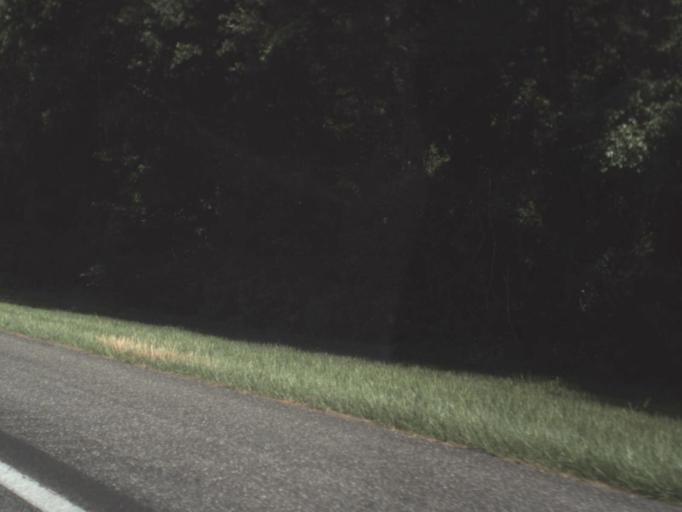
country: US
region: Florida
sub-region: Madison County
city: Madison
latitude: 30.4317
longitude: -83.6089
